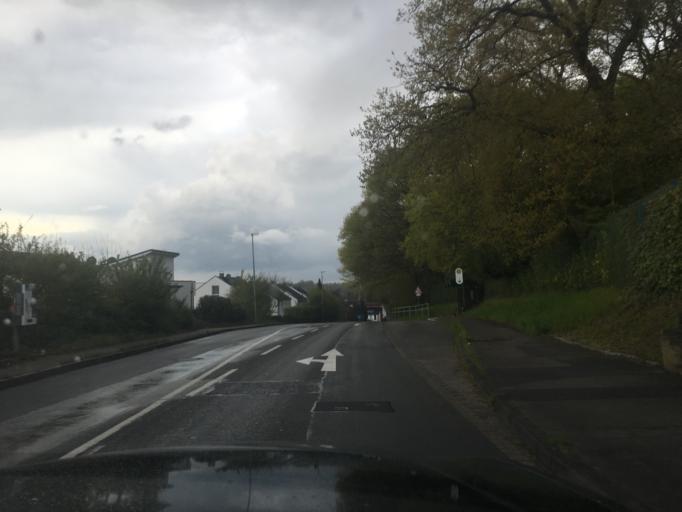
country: DE
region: North Rhine-Westphalia
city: Leichlingen
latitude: 51.1184
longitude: 7.0025
